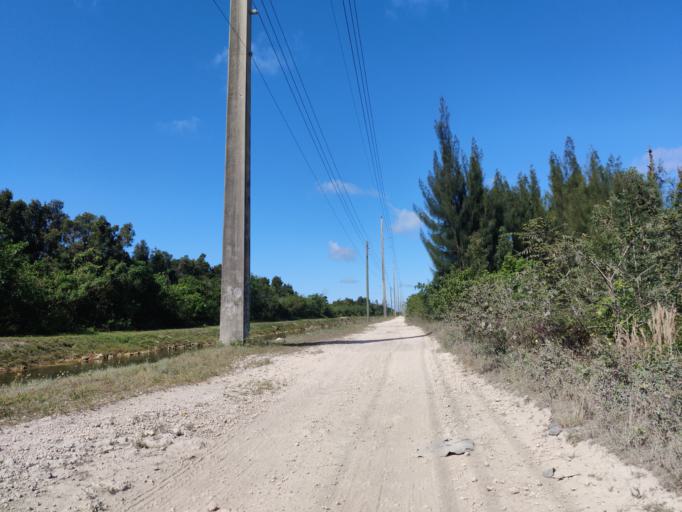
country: US
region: Florida
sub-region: Miami-Dade County
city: Kendall West
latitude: 25.7275
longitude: -80.4639
